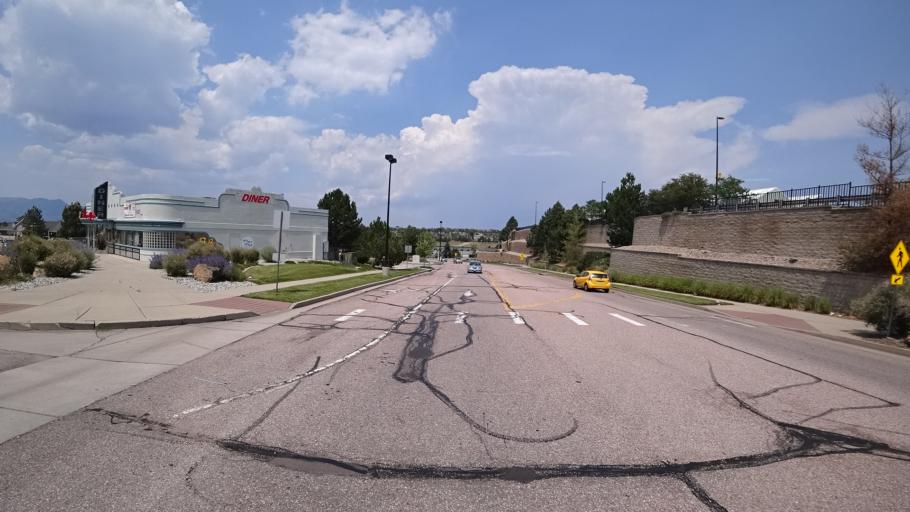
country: US
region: Colorado
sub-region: El Paso County
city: Black Forest
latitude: 38.9412
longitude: -104.7262
